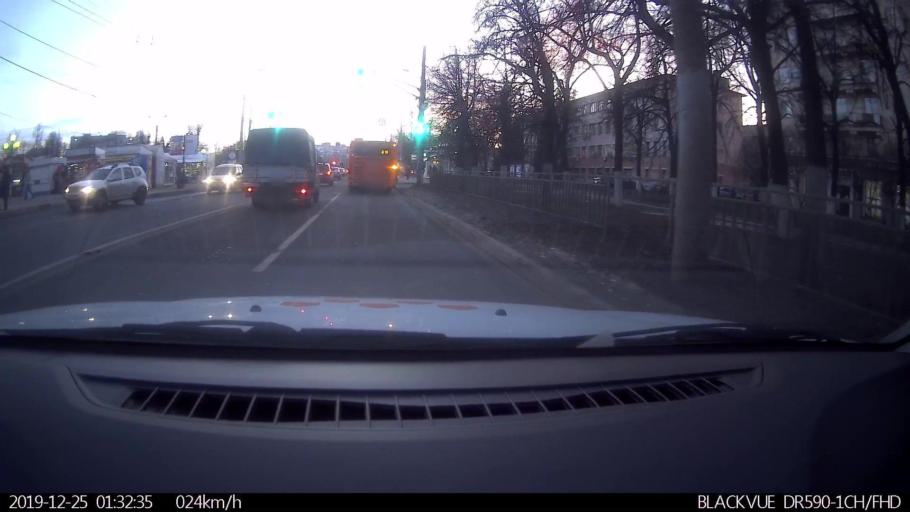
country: RU
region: Nizjnij Novgorod
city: Gorbatovka
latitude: 56.2432
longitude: 43.8636
